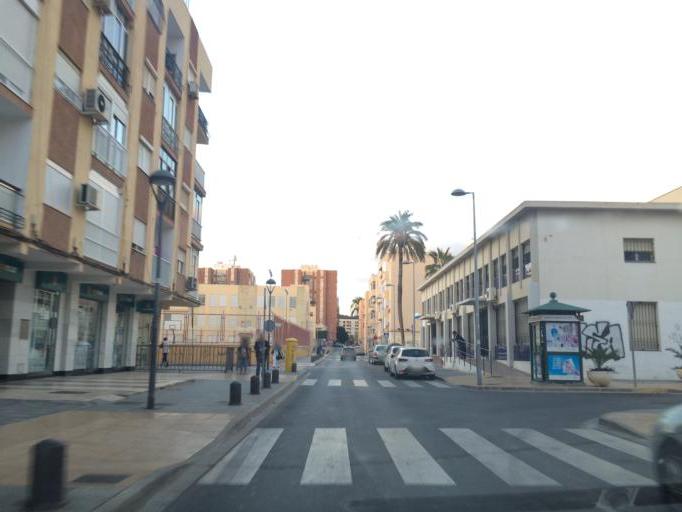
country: ES
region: Andalusia
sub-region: Provincia de Almeria
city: Almeria
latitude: 36.8326
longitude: -2.4491
